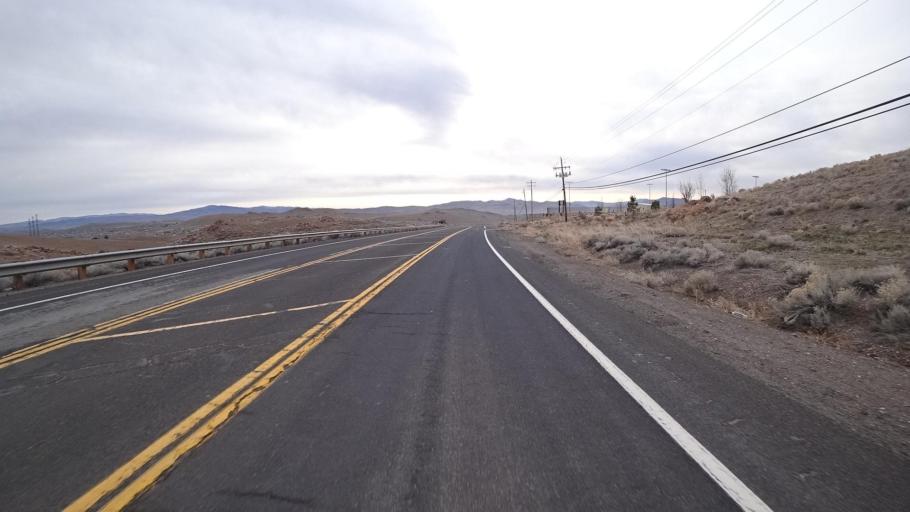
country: US
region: Nevada
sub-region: Washoe County
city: Sun Valley
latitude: 39.5746
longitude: -119.7930
